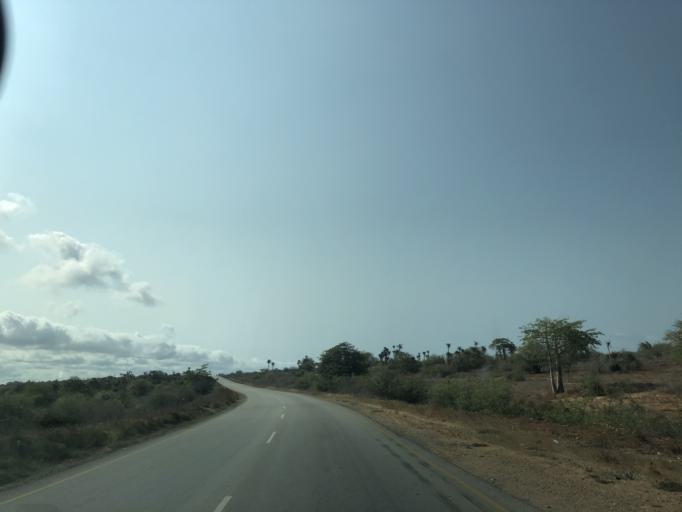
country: AO
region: Luanda
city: Luanda
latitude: -9.6986
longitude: 13.2114
